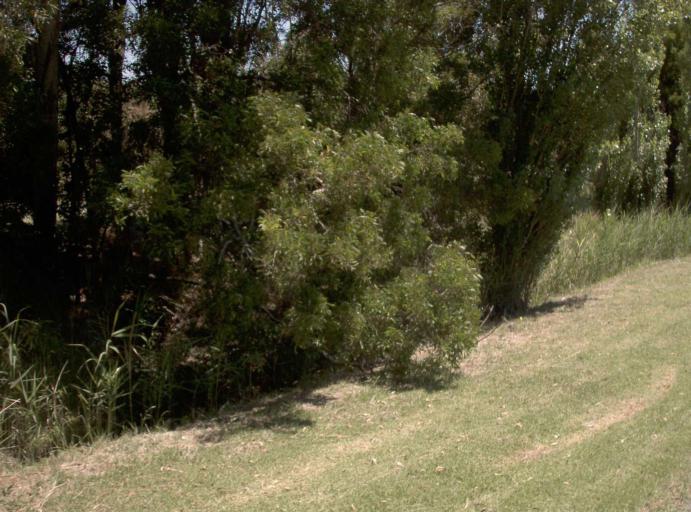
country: AU
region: Victoria
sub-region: Casey
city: Hallam
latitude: -38.0128
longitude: 145.2867
